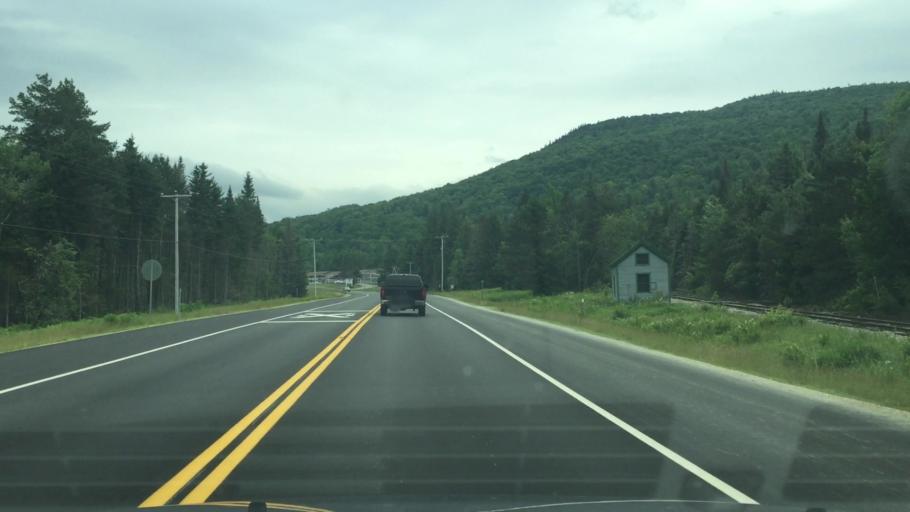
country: US
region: New Hampshire
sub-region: Coos County
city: Jefferson
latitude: 44.2591
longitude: -71.4548
